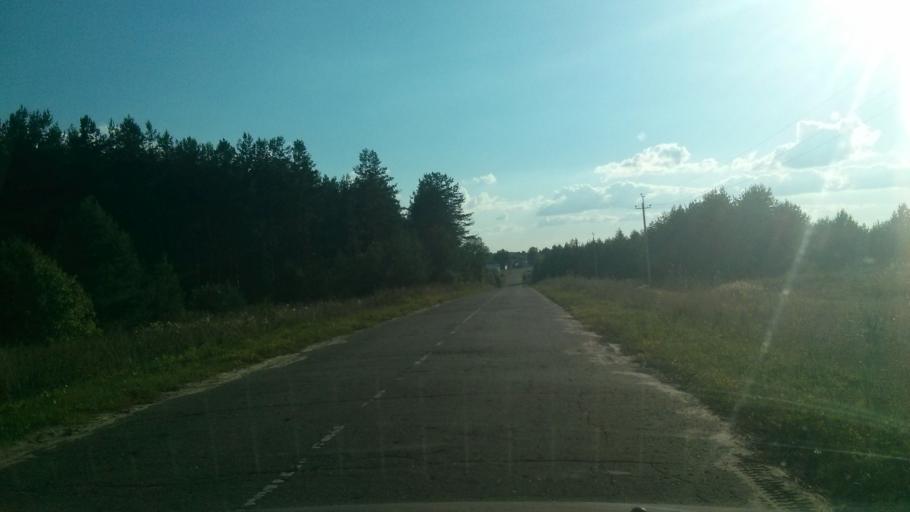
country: RU
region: Vladimir
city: Melenki
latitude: 55.2985
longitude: 41.8247
